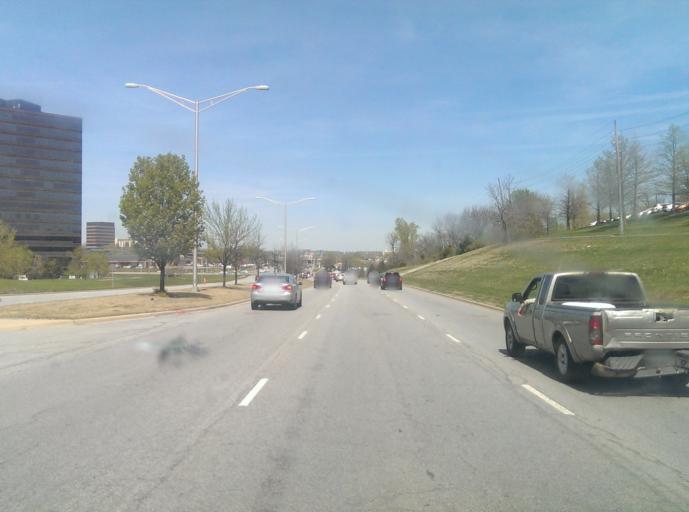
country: US
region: Kansas
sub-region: Johnson County
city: Overland Park
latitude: 38.9239
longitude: -94.6673
